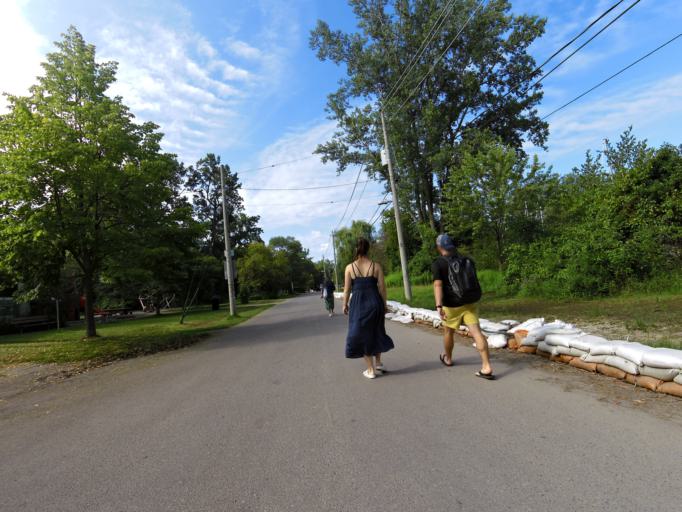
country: CA
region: Ontario
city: Toronto
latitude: 43.6286
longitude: -79.3564
